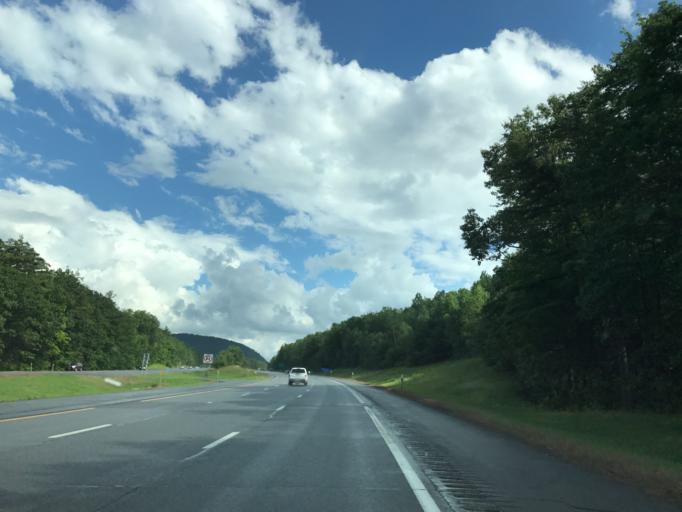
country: US
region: New York
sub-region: Warren County
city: Glens Falls North
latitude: 43.4106
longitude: -73.7214
